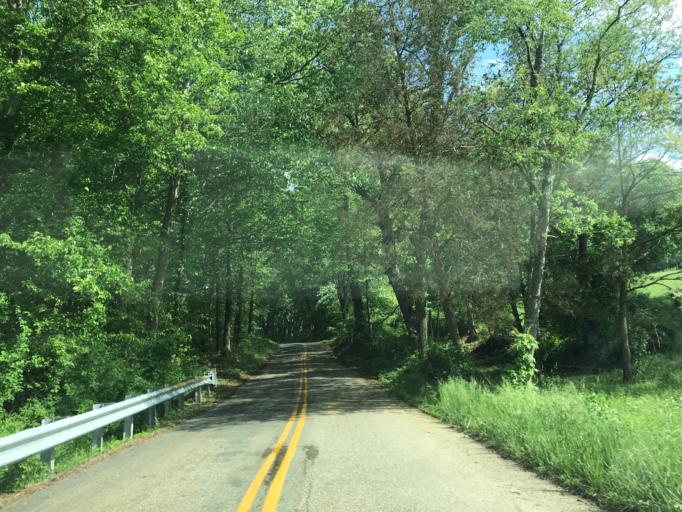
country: US
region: Maryland
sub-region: Harford County
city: Bel Air North
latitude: 39.6125
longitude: -76.3705
